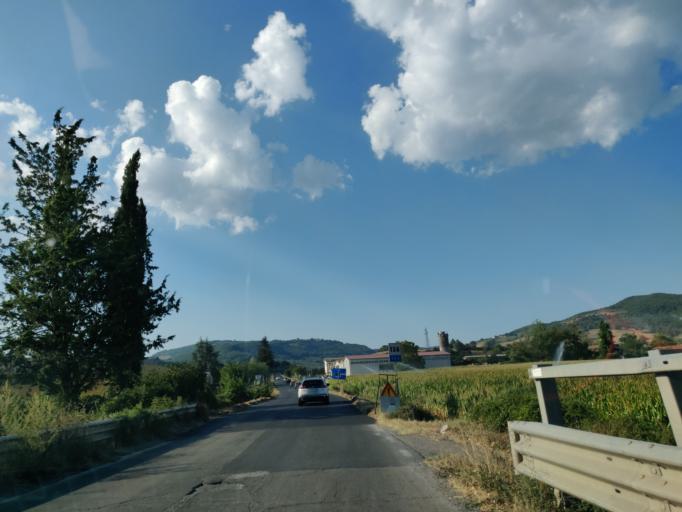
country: IT
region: Latium
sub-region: Provincia di Viterbo
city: Acquapendente
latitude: 42.7654
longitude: 11.8563
